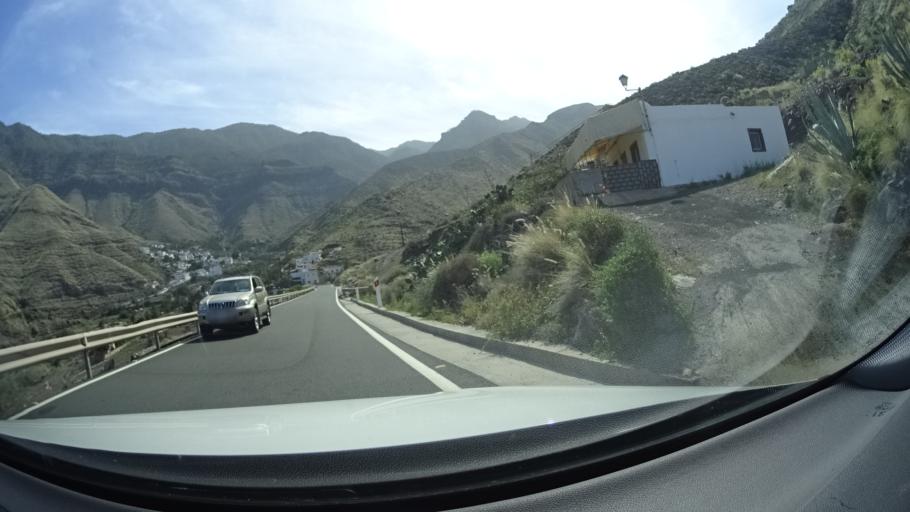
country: ES
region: Canary Islands
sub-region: Provincia de Las Palmas
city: Agaete
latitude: 28.0465
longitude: -15.7331
